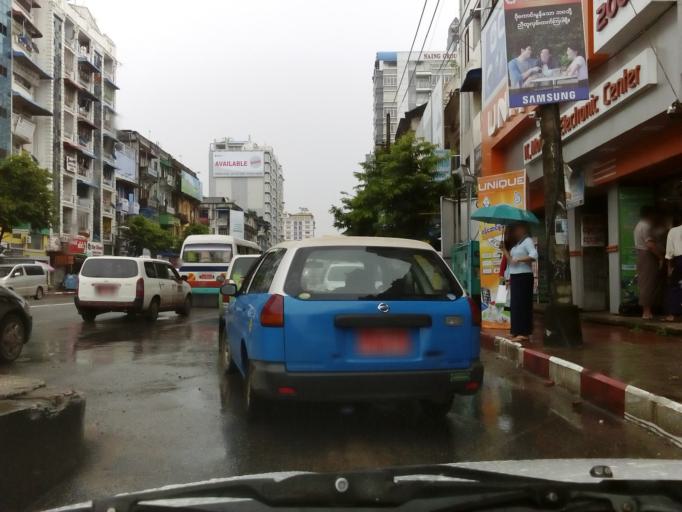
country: MM
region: Yangon
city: Yangon
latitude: 16.7779
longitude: 96.1617
